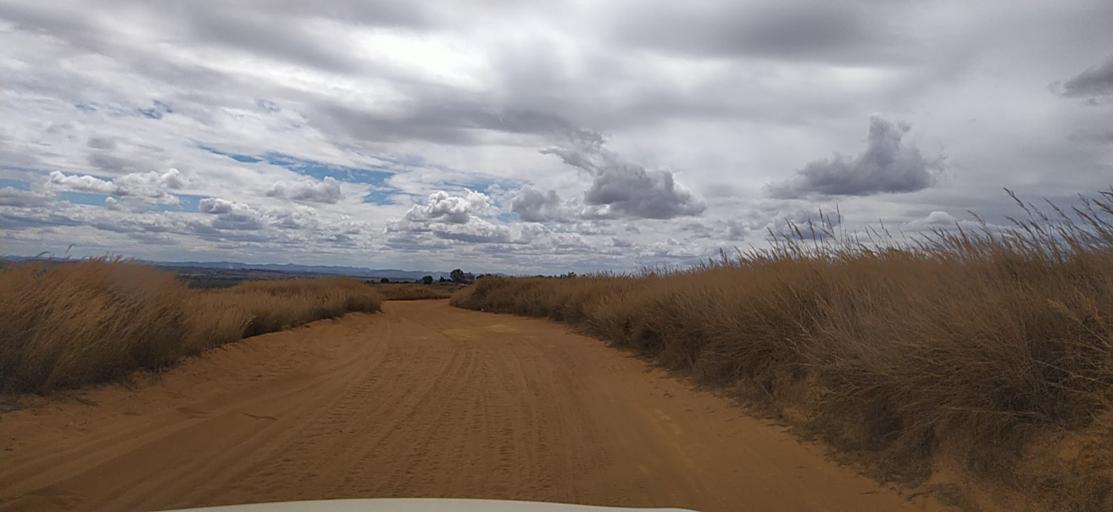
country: MG
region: Alaotra Mangoro
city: Ambatondrazaka
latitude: -17.9050
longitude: 48.2601
